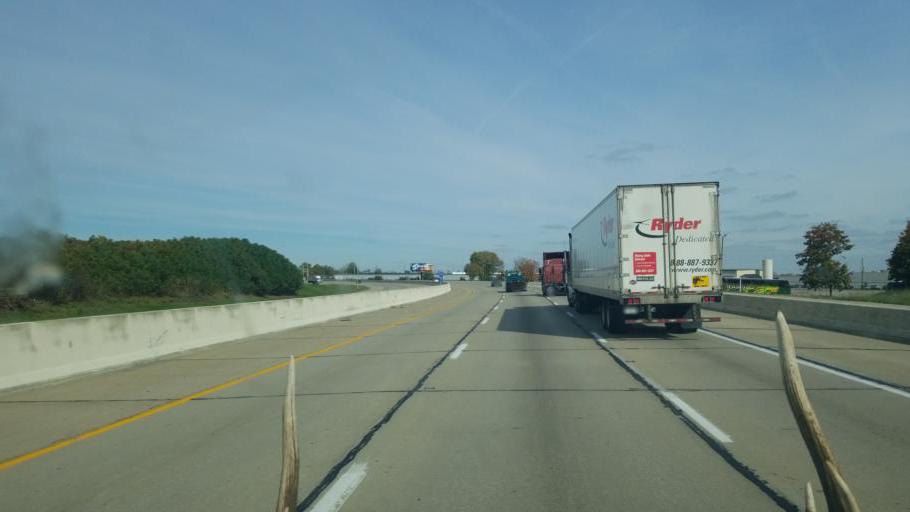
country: US
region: Indiana
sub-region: Marion County
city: Speedway
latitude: 39.7316
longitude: -86.2415
